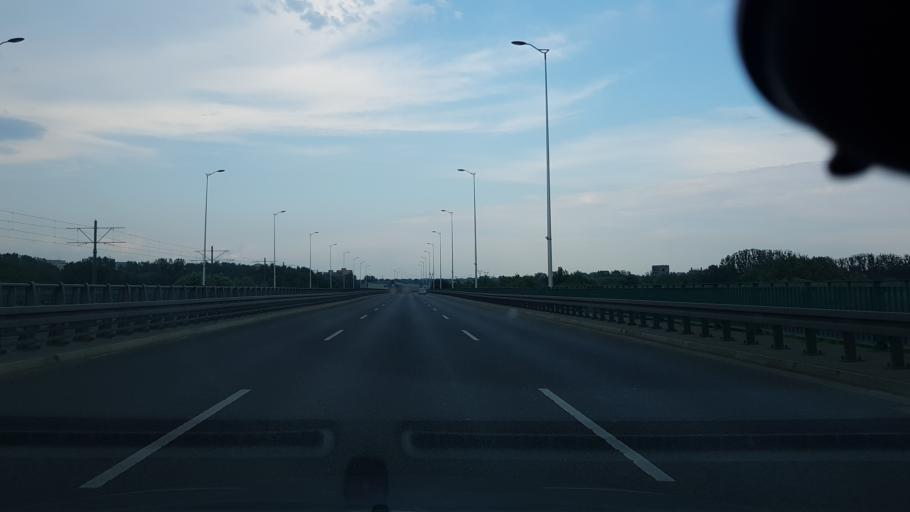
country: PL
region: Masovian Voivodeship
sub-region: Warszawa
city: Bielany
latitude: 52.3072
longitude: 20.9526
